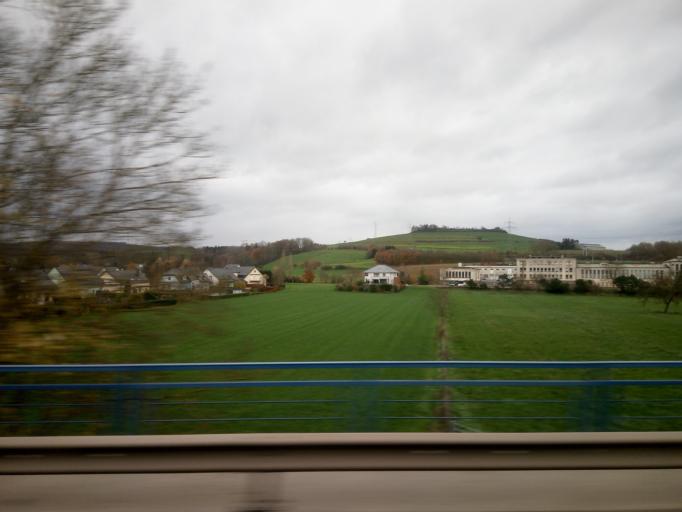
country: LU
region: Diekirch
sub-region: Canton de Diekirch
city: Ettelbruck
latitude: 49.8503
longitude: 6.1159
